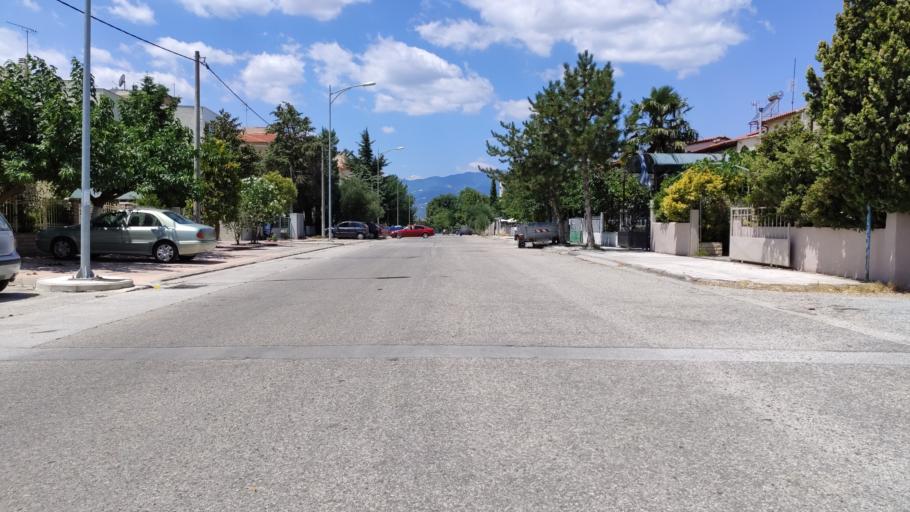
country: GR
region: East Macedonia and Thrace
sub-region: Nomos Rodopis
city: Komotini
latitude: 41.1251
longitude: 25.3997
